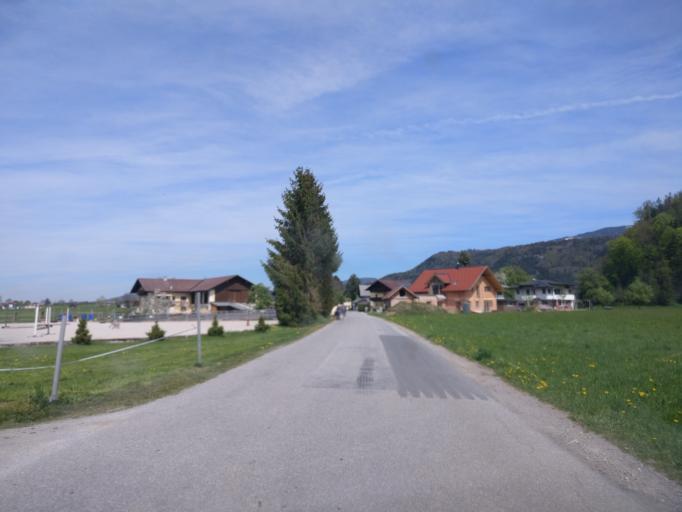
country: AT
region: Salzburg
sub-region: Politischer Bezirk Hallein
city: Kuchl
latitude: 47.6328
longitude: 13.1549
